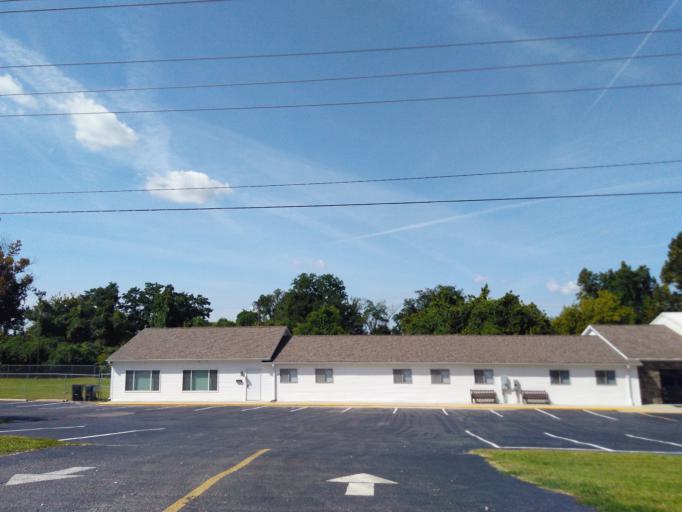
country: US
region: Illinois
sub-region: Saint Clair County
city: Caseyville
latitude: 38.6494
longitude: -90.0184
